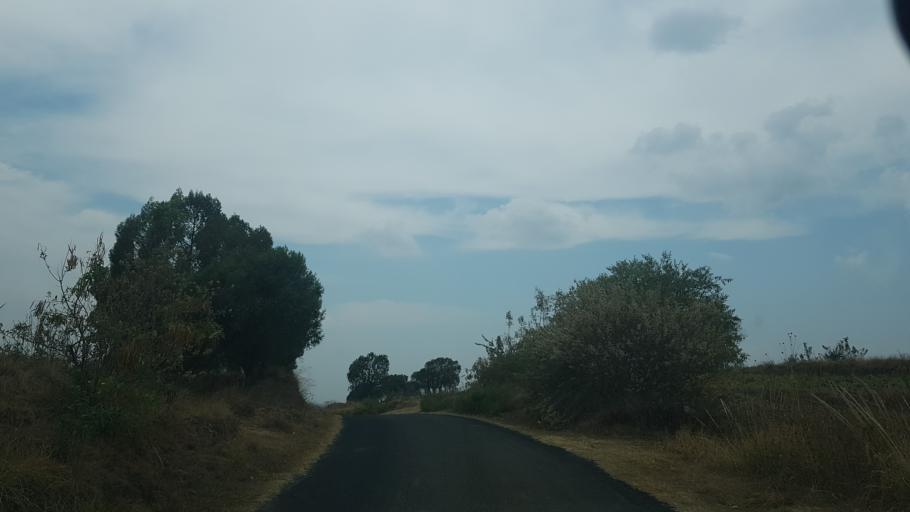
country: MX
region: Puebla
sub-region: Atzitzihuacan
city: Santiago Atzitzihuacan
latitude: 18.8372
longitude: -98.6179
